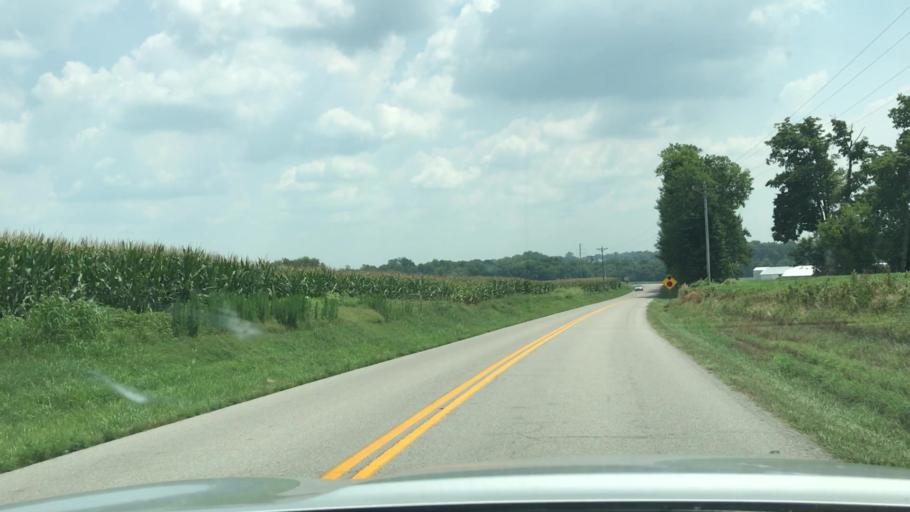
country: US
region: Kentucky
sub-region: Todd County
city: Elkton
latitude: 36.7266
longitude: -87.0893
